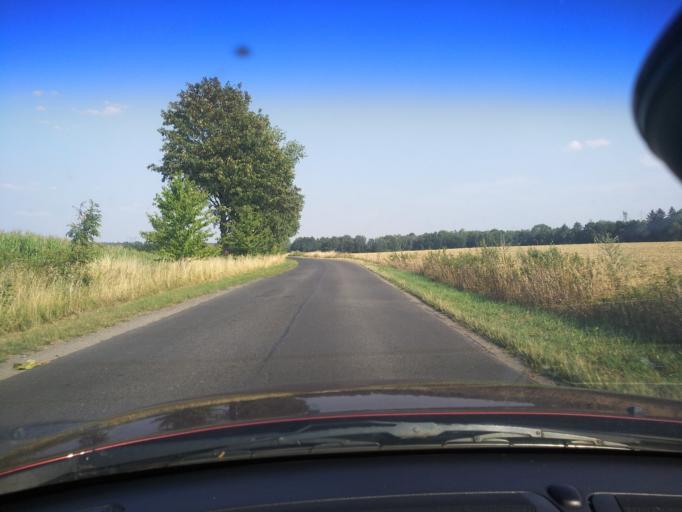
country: PL
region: Lower Silesian Voivodeship
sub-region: Powiat zgorzelecki
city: Sulikow
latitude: 51.0994
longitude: 15.0746
